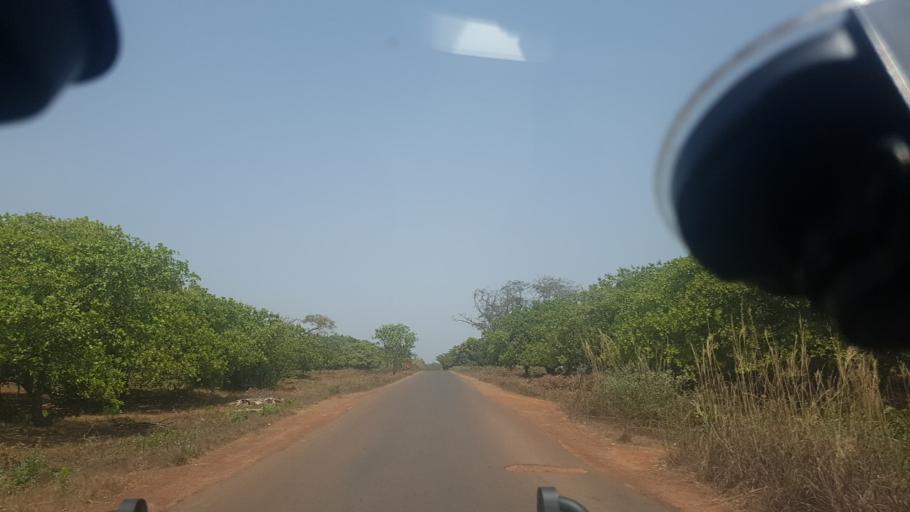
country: GW
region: Oio
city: Bissora
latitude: 12.3029
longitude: -15.7636
